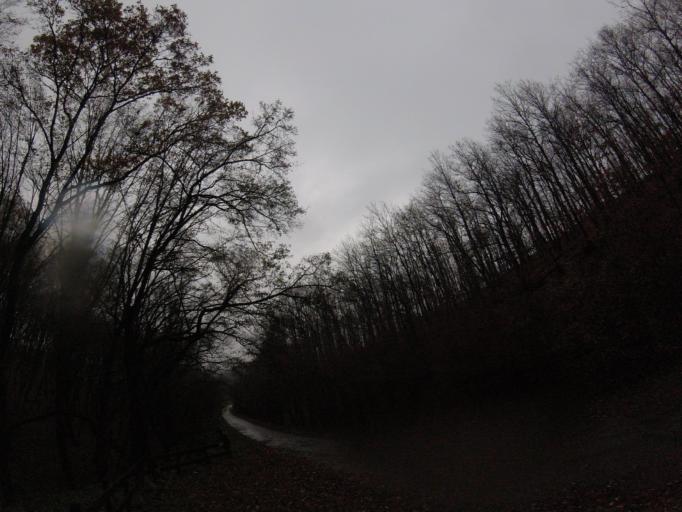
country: HU
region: Nograd
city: Rimoc
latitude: 47.9982
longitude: 19.5731
